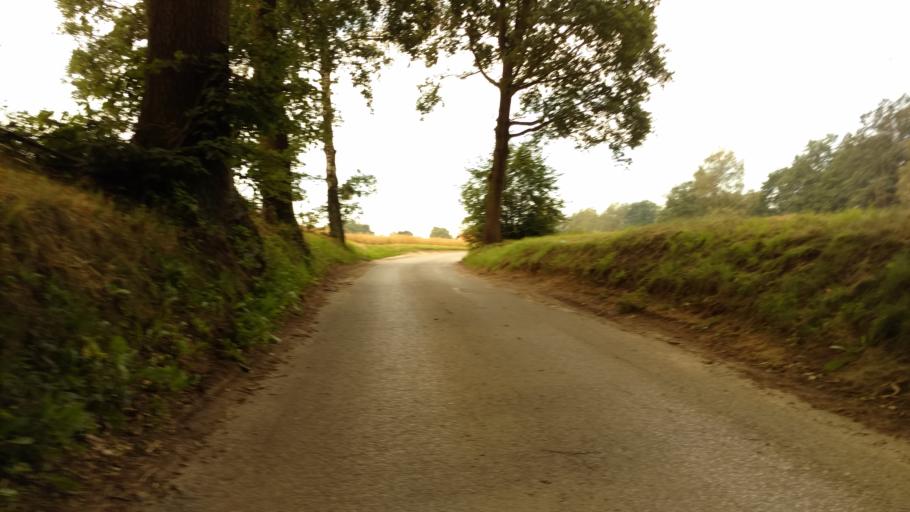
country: PL
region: Silesian Voivodeship
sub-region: Powiat pszczynski
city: Jankowice
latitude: 49.9940
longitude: 19.0116
